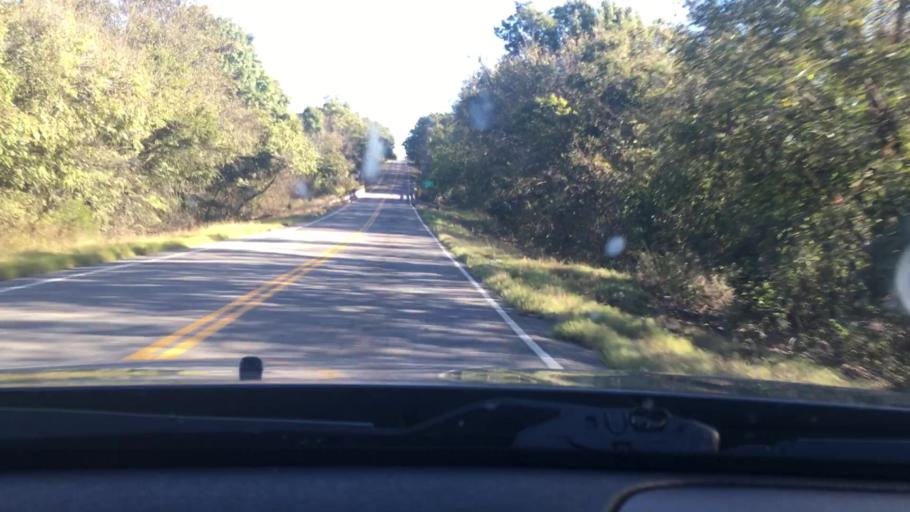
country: US
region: Oklahoma
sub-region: Marshall County
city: Madill
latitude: 34.0995
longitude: -96.7568
